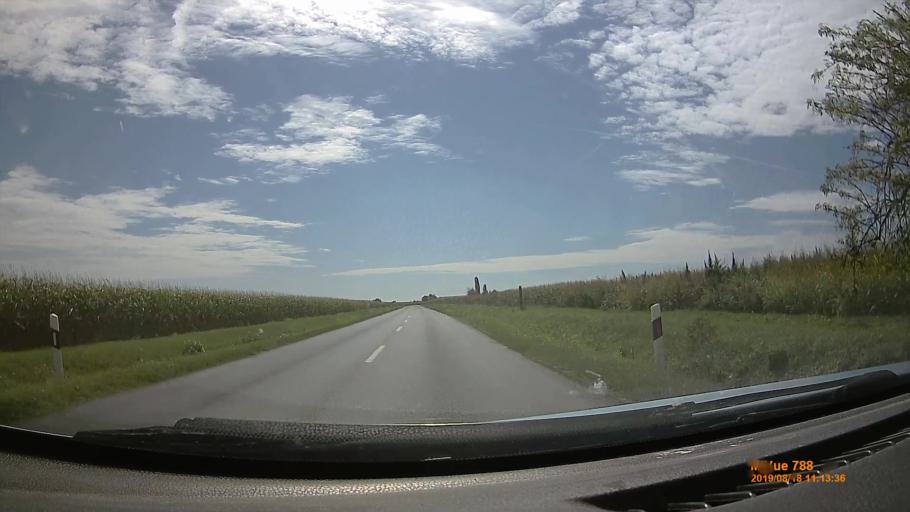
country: HU
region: Fejer
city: Szabadbattyan
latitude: 47.0992
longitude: 18.3886
